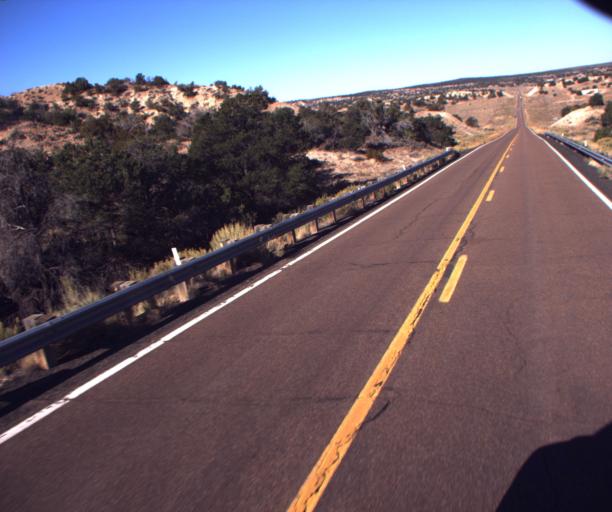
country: US
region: Arizona
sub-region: Navajo County
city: First Mesa
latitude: 35.7597
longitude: -109.9655
